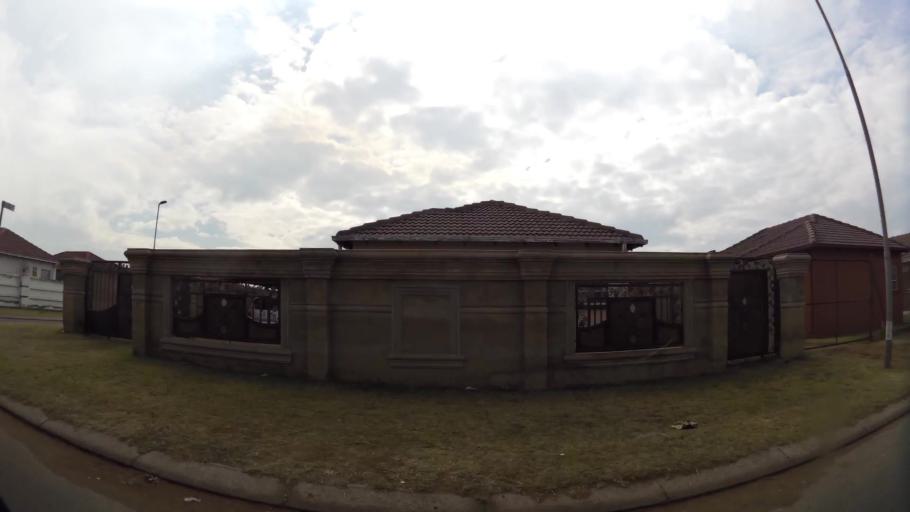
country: ZA
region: Gauteng
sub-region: Sedibeng District Municipality
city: Vanderbijlpark
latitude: -26.6849
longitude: 27.8424
